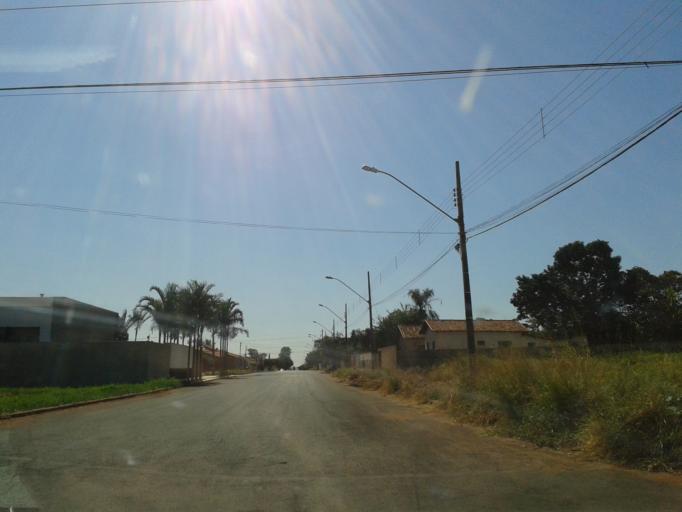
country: BR
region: Minas Gerais
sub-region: Ituiutaba
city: Ituiutaba
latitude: -18.9940
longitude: -49.4594
